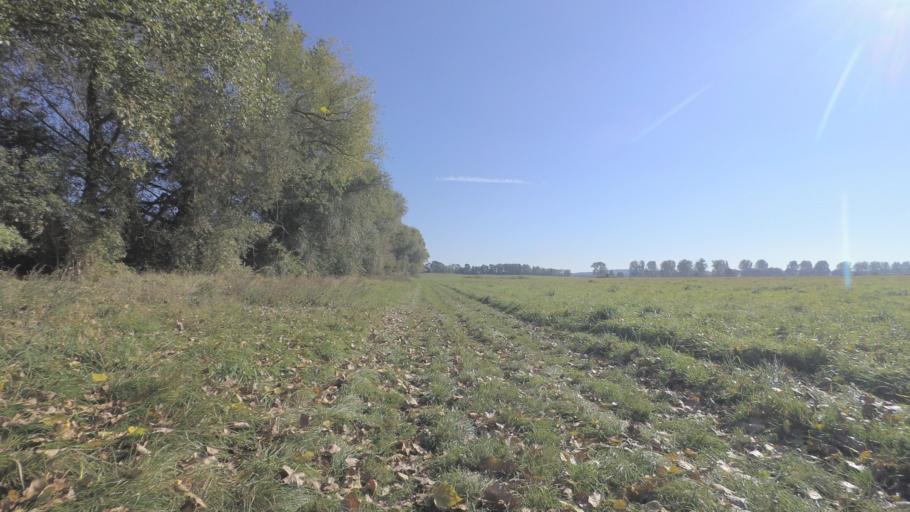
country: DE
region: Brandenburg
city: Rangsdorf
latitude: 52.2977
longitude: 13.3653
